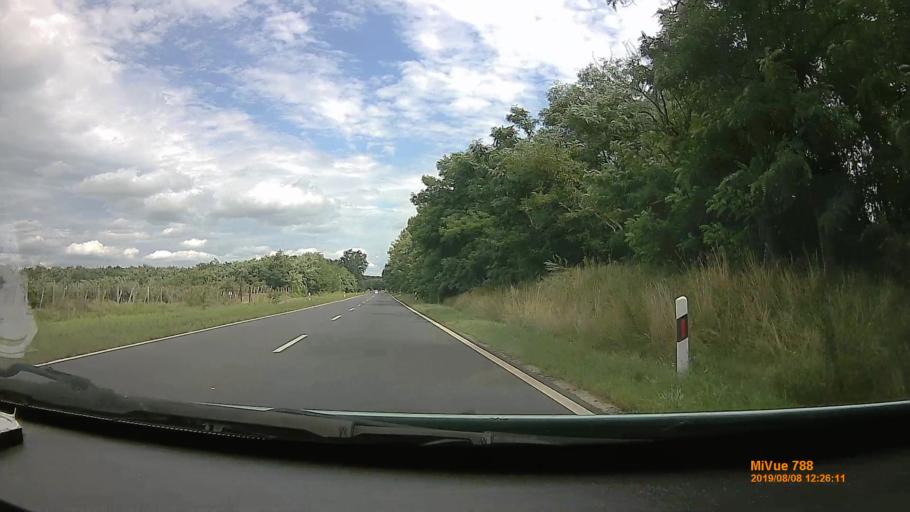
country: HU
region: Szabolcs-Szatmar-Bereg
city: Nyirbogat
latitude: 47.8158
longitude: 22.0845
